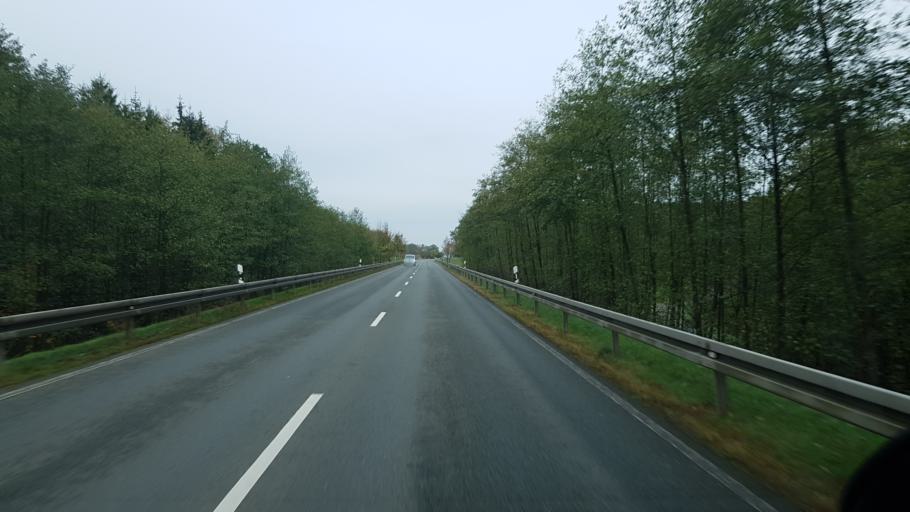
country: DE
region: Saxony
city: Lichtentanne
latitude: 50.6569
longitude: 12.4098
